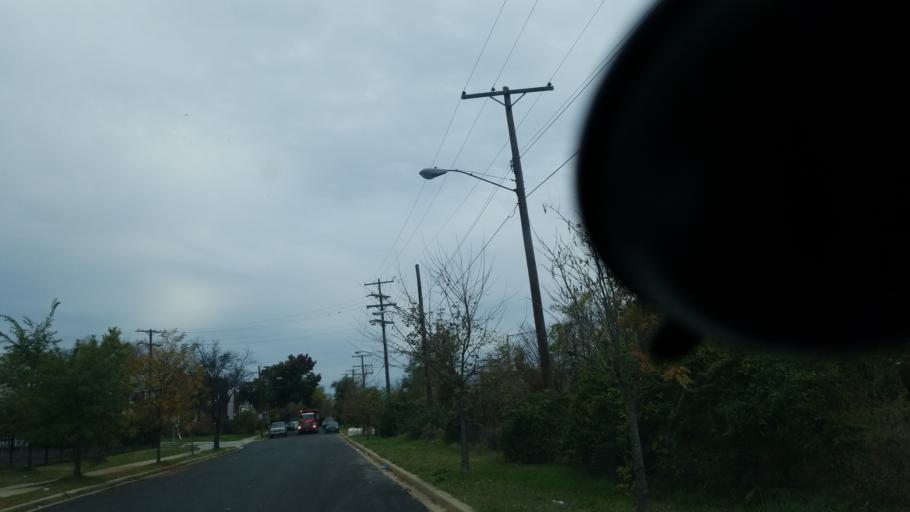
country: US
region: Maryland
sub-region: Prince George's County
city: Hillcrest Heights
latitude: 38.8725
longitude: -76.9802
